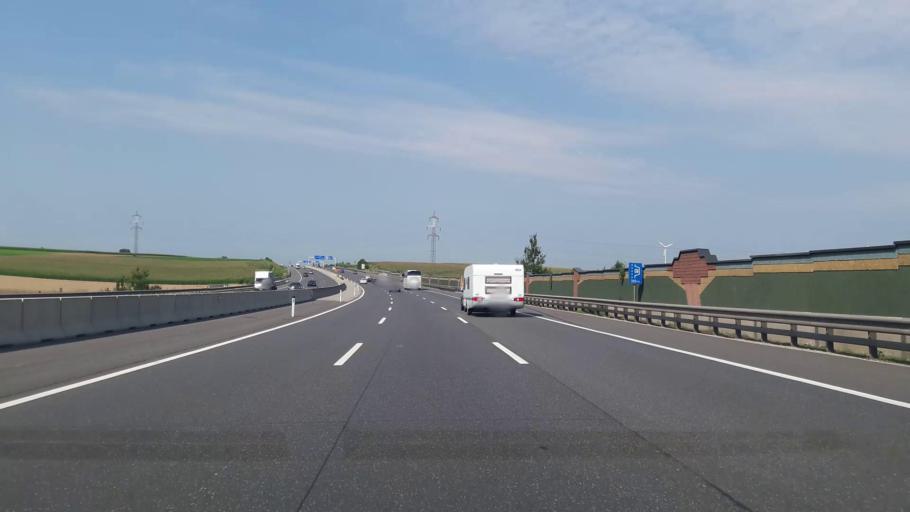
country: AT
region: Lower Austria
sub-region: Politischer Bezirk Sankt Polten
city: Pyhra
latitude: 48.1850
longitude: 15.6831
